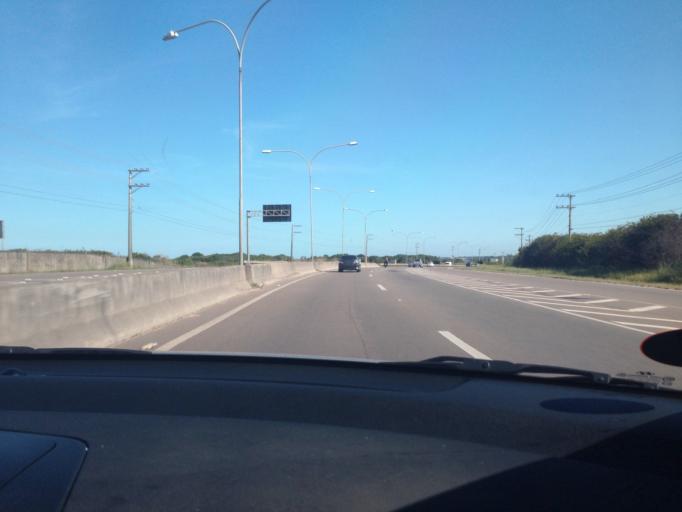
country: BR
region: Espirito Santo
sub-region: Vila Velha
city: Vila Velha
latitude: -20.4500
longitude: -40.3345
